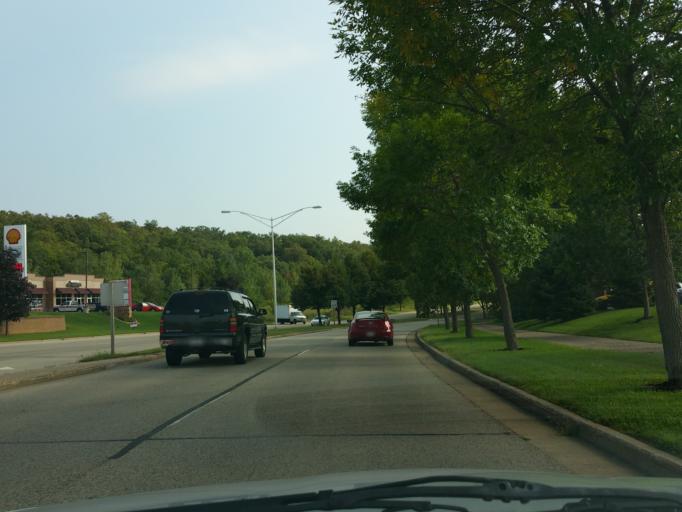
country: US
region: Wisconsin
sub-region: Saint Croix County
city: Hudson
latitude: 44.9539
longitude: -92.7211
